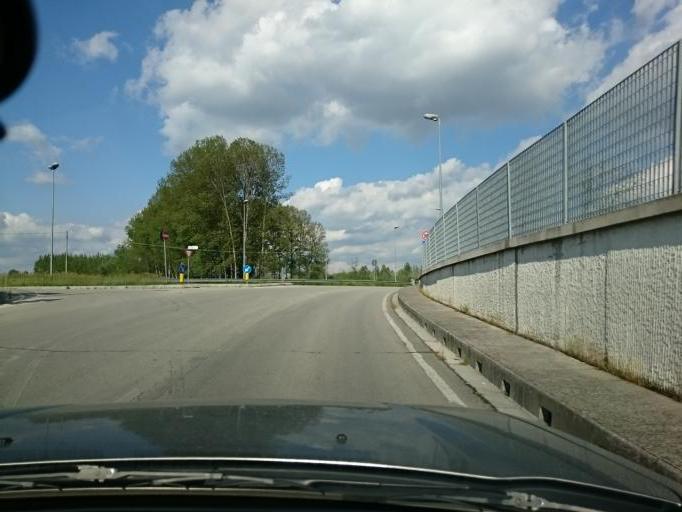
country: IT
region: Veneto
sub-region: Provincia di Padova
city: Trebaseleghe
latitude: 45.5922
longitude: 12.0245
